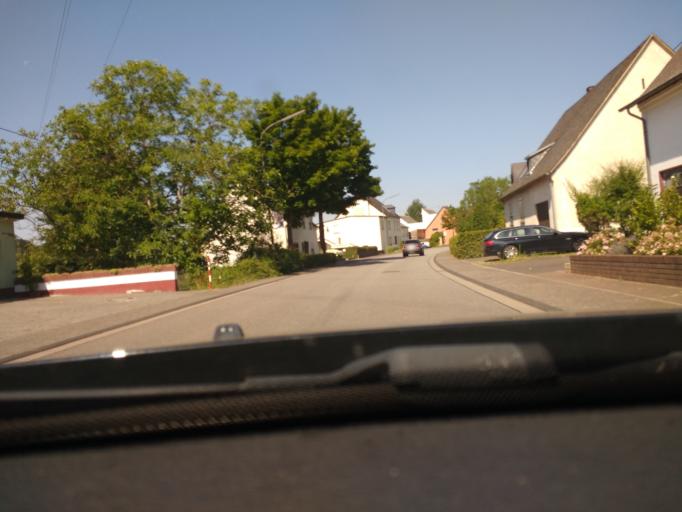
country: DE
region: Rheinland-Pfalz
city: Bausendorf
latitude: 50.0123
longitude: 7.0009
